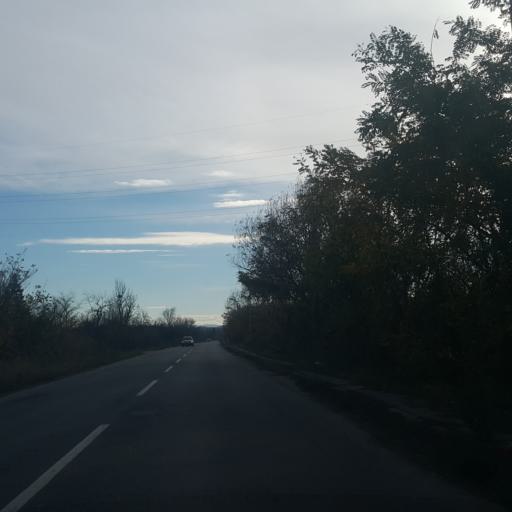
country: RS
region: Central Serbia
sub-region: Belgrade
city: Lazarevac
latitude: 44.4244
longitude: 20.2782
